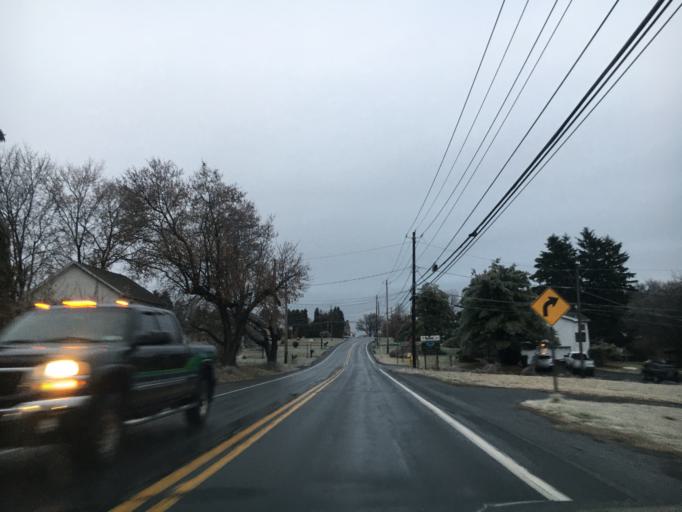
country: US
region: Pennsylvania
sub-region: Lehigh County
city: Schnecksville
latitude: 40.6188
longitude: -75.6411
